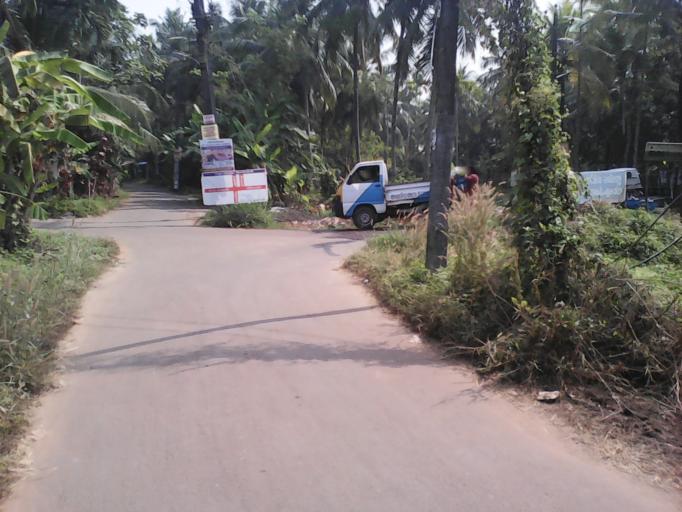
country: IN
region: Kerala
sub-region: Kozhikode
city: Kozhikode
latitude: 11.2805
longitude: 75.8186
